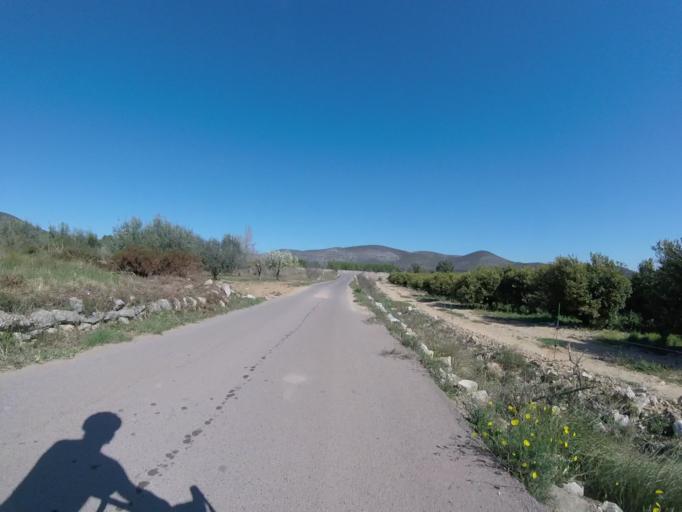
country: ES
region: Valencia
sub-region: Provincia de Castello
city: Santa Magdalena de Pulpis
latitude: 40.3591
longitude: 0.2858
